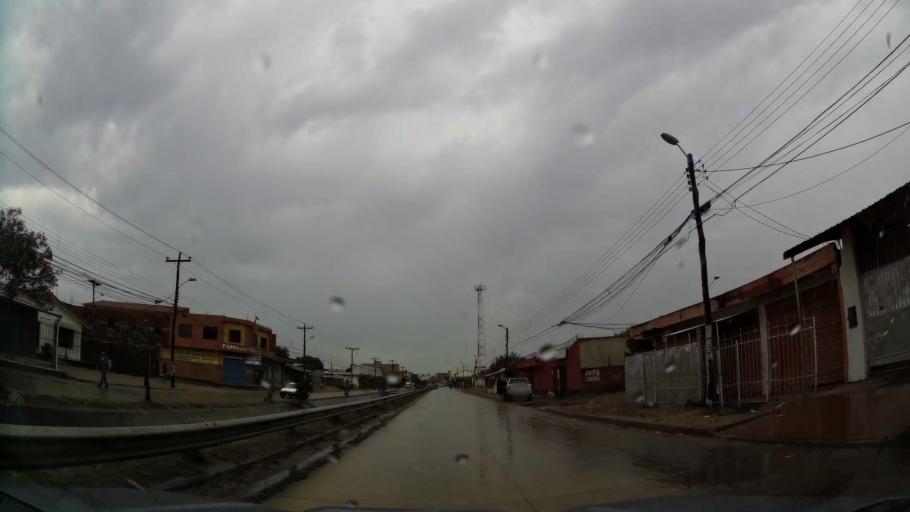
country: BO
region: Santa Cruz
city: Santa Cruz de la Sierra
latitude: -17.8049
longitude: -63.1357
